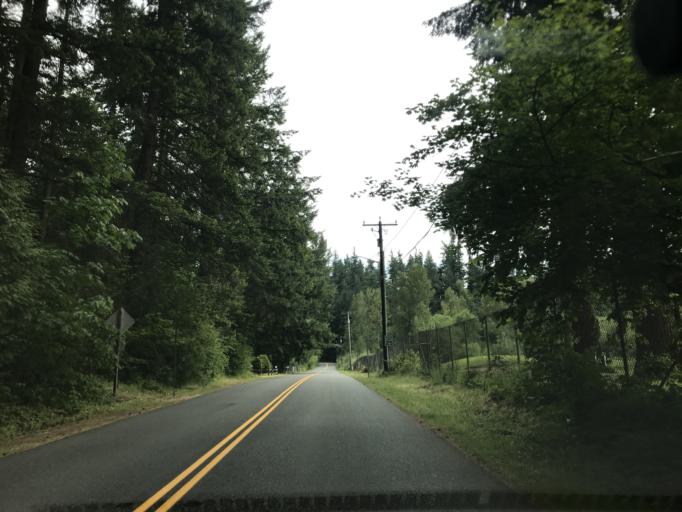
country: US
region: Washington
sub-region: King County
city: Maple Valley
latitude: 47.3787
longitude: -122.0426
